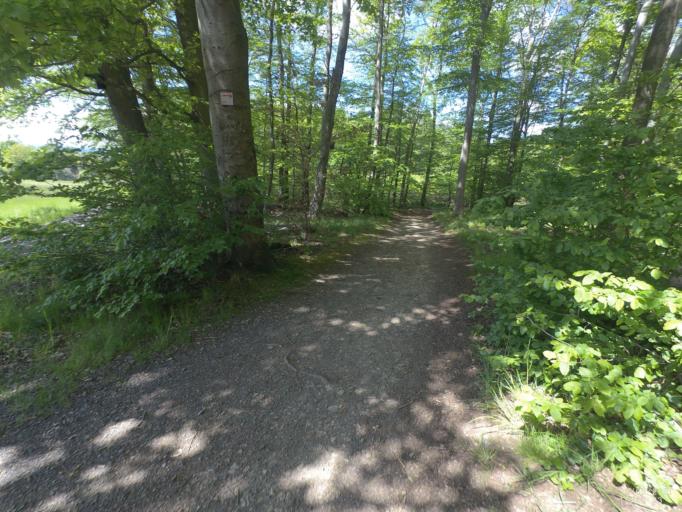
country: DE
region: Rheinland-Pfalz
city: Waldesch
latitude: 50.2844
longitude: 7.5542
